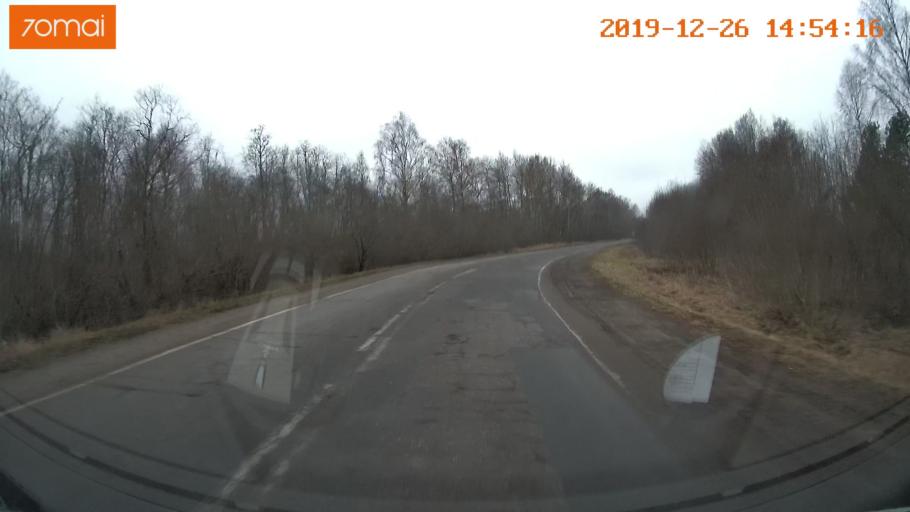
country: RU
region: Jaroslavl
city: Rybinsk
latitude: 58.3084
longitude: 38.8856
